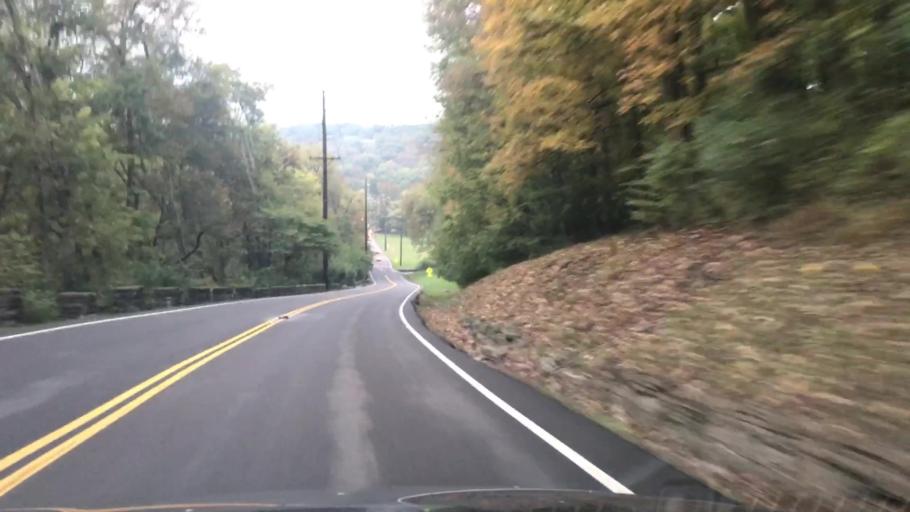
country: US
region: Tennessee
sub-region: Davidson County
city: Belle Meade
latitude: 36.0585
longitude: -86.9025
